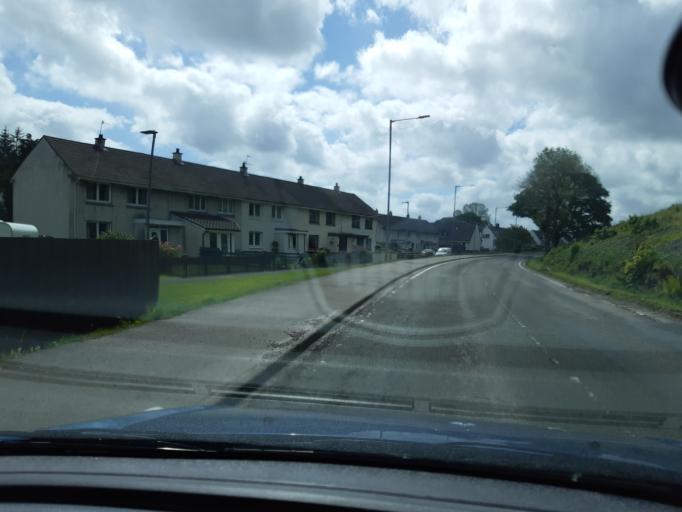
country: GB
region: Scotland
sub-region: Argyll and Bute
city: Lochgilphead
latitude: 56.0411
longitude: -5.4401
